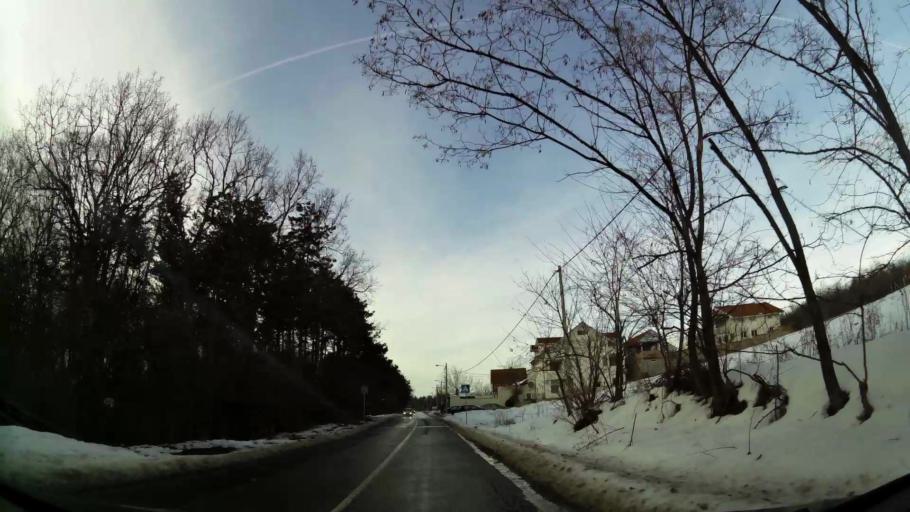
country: RS
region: Central Serbia
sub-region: Belgrade
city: Zvezdara
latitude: 44.7304
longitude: 20.5116
